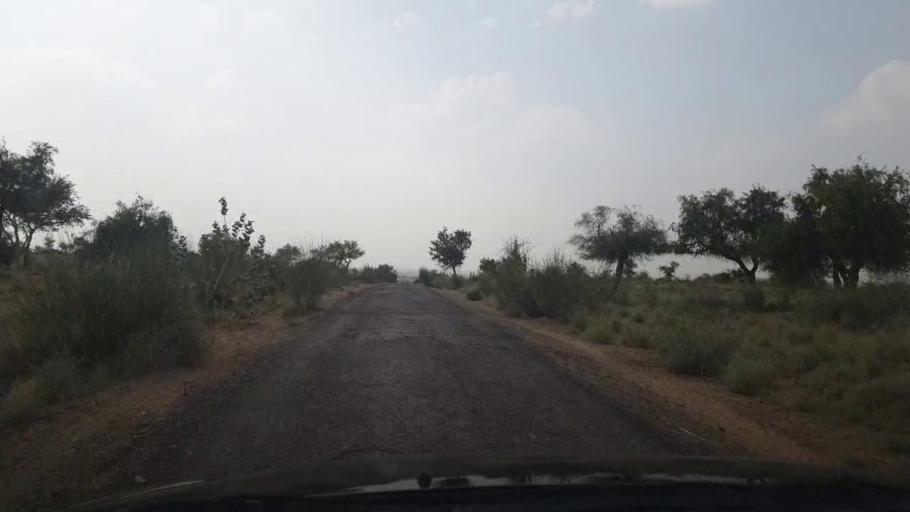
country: PK
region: Sindh
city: Islamkot
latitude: 24.9688
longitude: 70.5974
